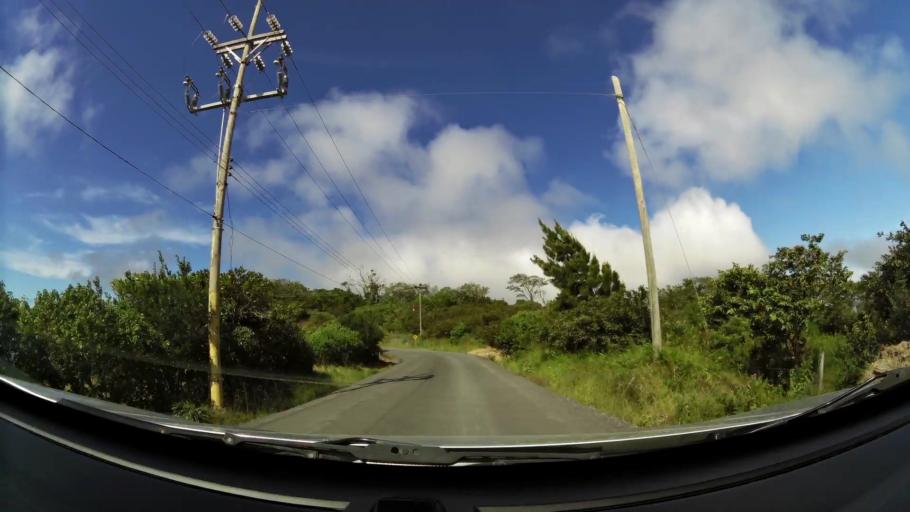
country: CR
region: Guanacaste
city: Juntas
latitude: 10.3399
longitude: -84.8923
